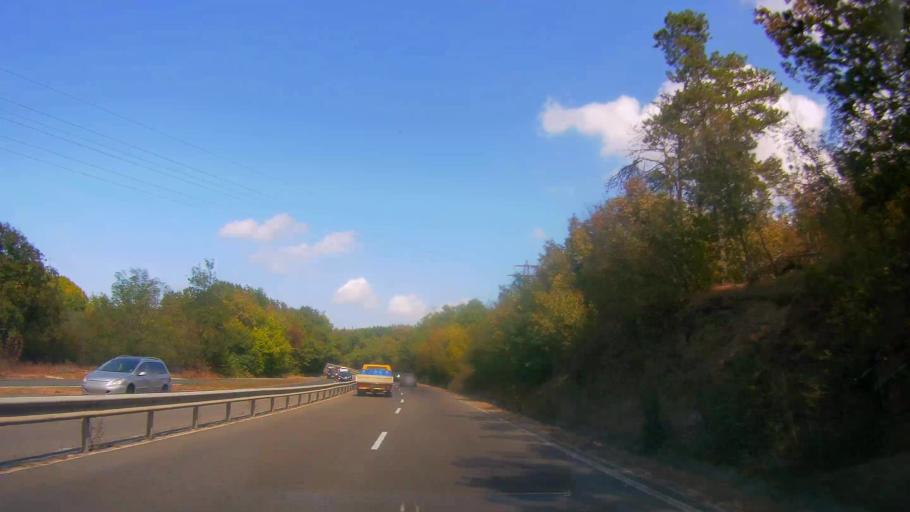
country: BG
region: Burgas
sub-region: Obshtina Burgas
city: Burgas
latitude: 42.4278
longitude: 27.5200
